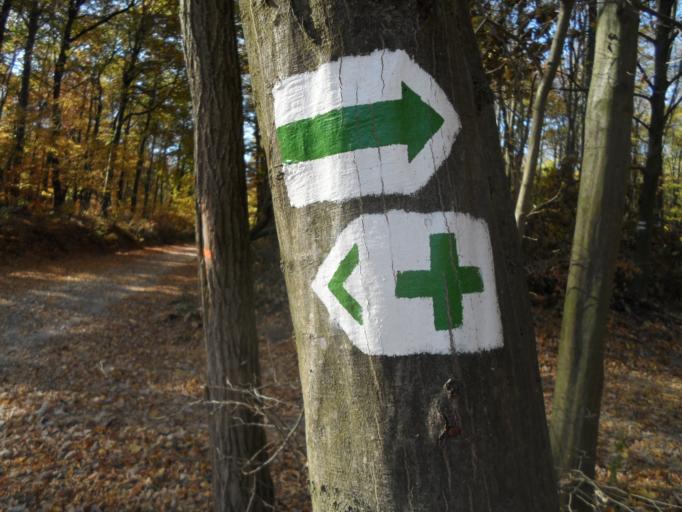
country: HU
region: Veszprem
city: Ajka
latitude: 47.1987
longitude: 17.5697
